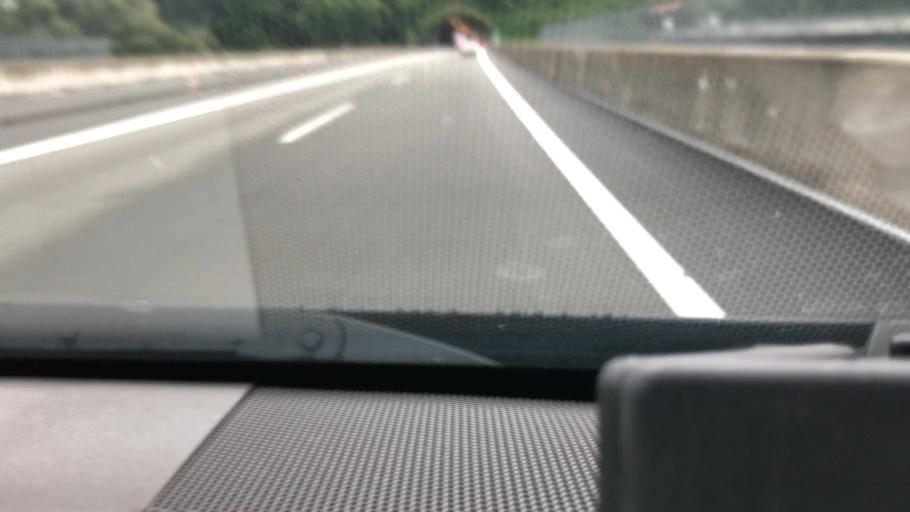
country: JP
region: Shizuoka
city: Shimada
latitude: 34.8722
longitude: 138.1682
